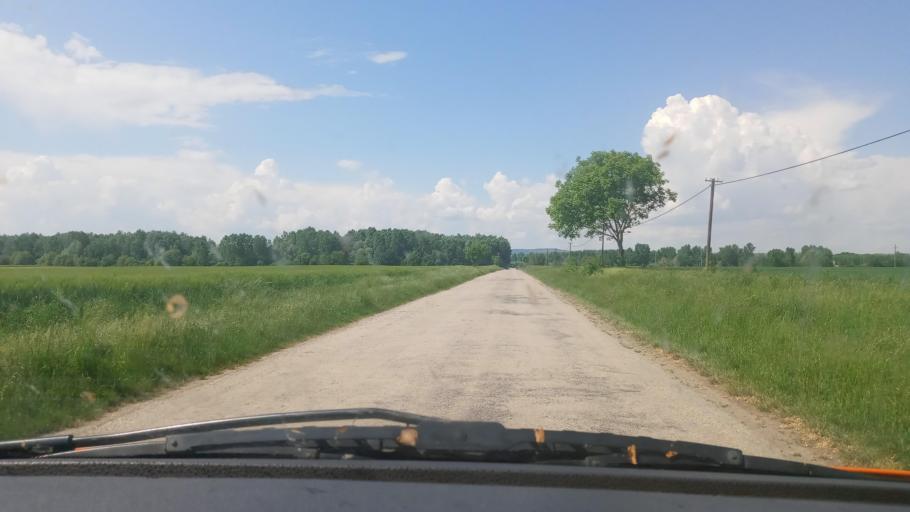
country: HU
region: Baranya
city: Siklos
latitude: 45.8064
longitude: 18.3434
